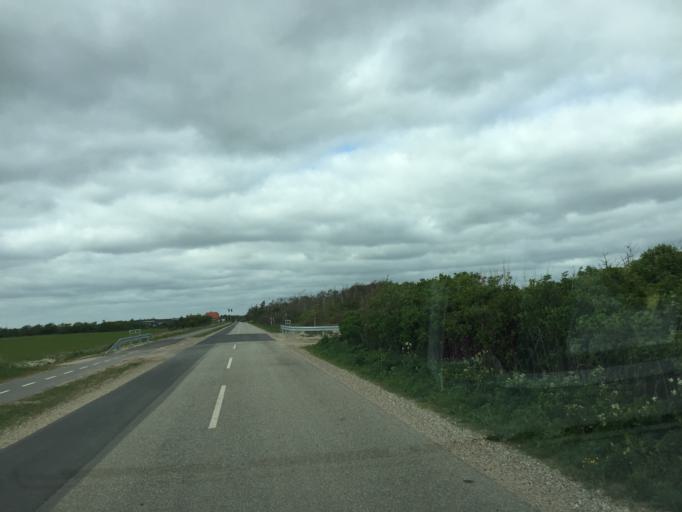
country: DK
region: Central Jutland
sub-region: Ringkobing-Skjern Kommune
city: Ringkobing
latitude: 56.0340
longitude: 8.3159
